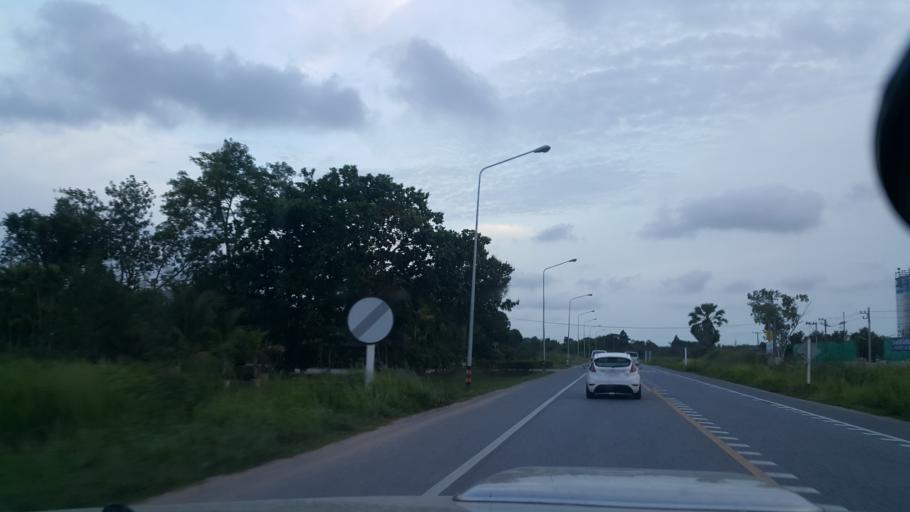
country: TH
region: Rayong
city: Ban Chang
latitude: 12.7121
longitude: 101.0038
